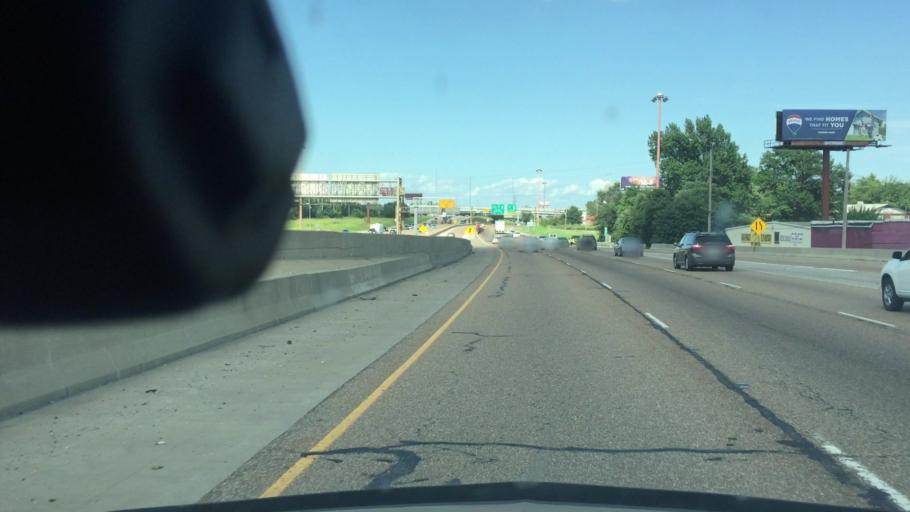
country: US
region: Illinois
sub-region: Saint Clair County
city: East Saint Louis
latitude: 38.6298
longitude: -90.1555
